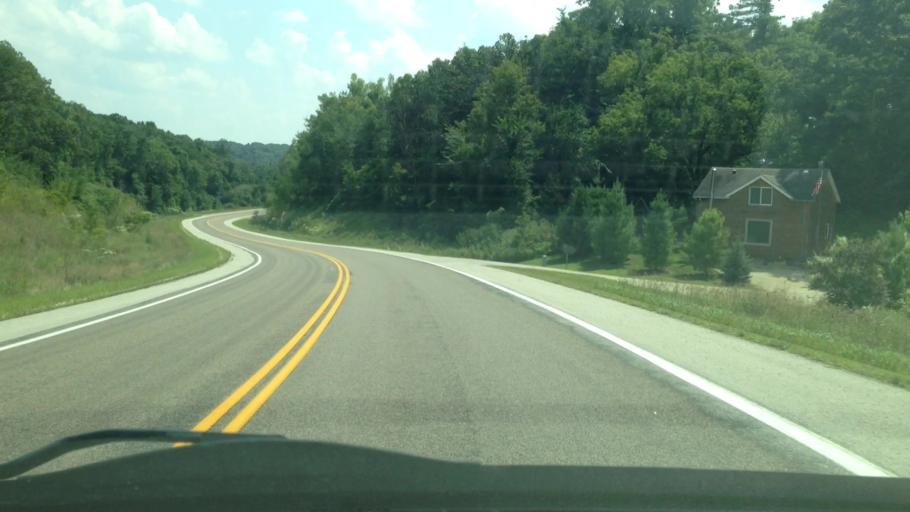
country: US
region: Minnesota
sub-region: Olmsted County
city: Stewartville
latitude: 43.8949
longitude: -92.4108
